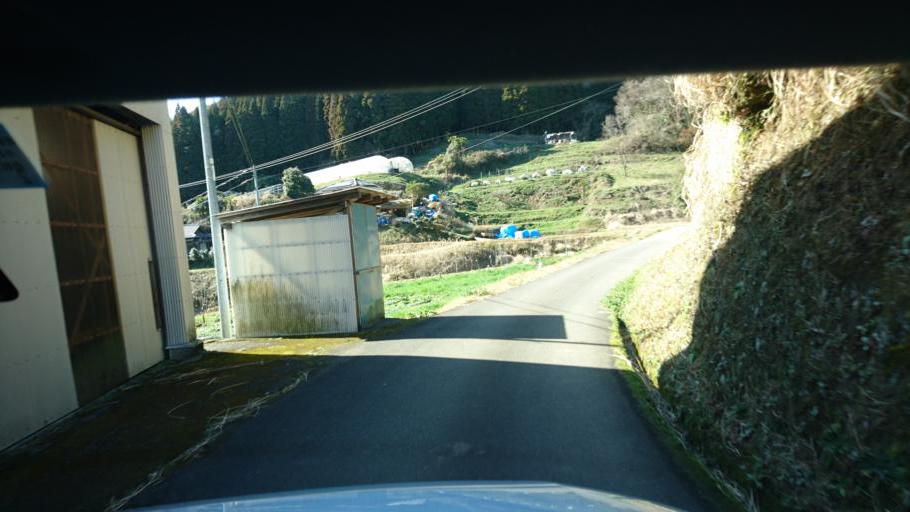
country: JP
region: Oita
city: Takedamachi
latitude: 32.7217
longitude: 131.3034
